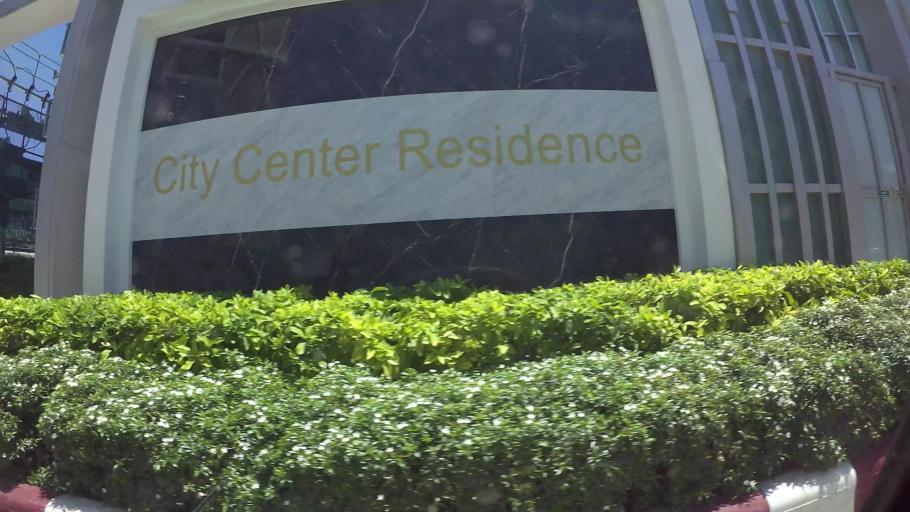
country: TH
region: Chon Buri
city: Phatthaya
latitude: 12.9278
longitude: 100.8900
